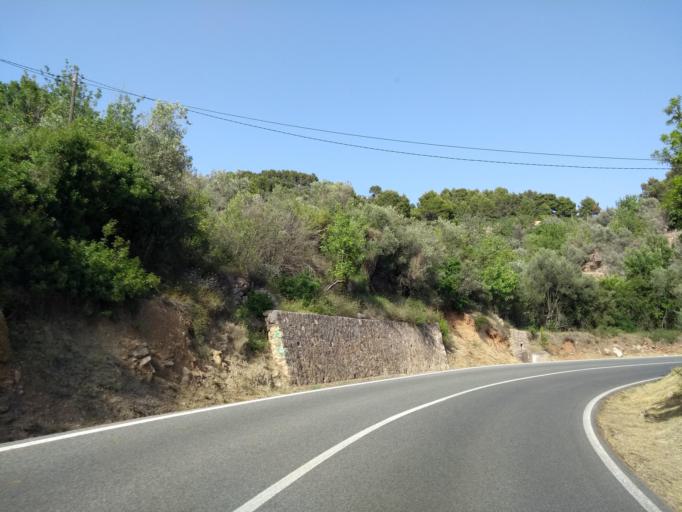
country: ES
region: Balearic Islands
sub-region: Illes Balears
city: Soller
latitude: 39.7828
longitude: 2.7156
